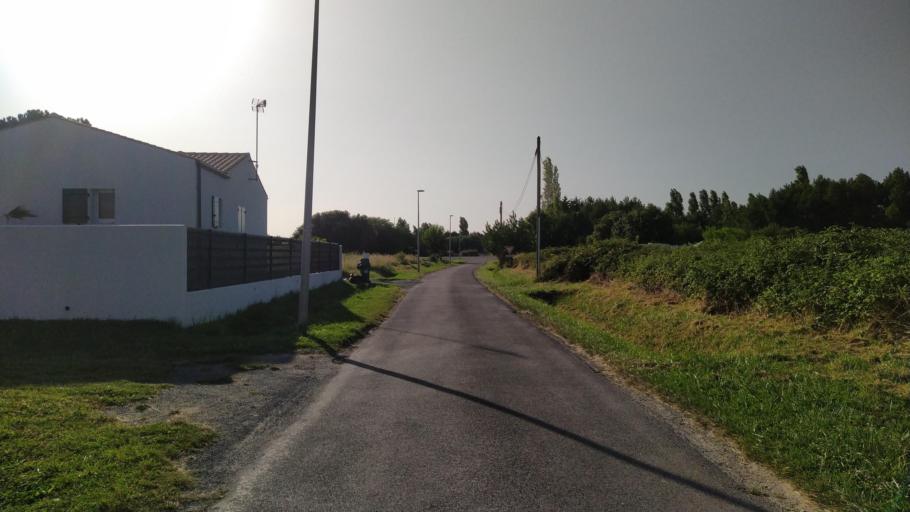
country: FR
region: Poitou-Charentes
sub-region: Departement de la Charente-Maritime
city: Saint-Trojan-les-Bains
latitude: 45.8632
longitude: -1.2318
